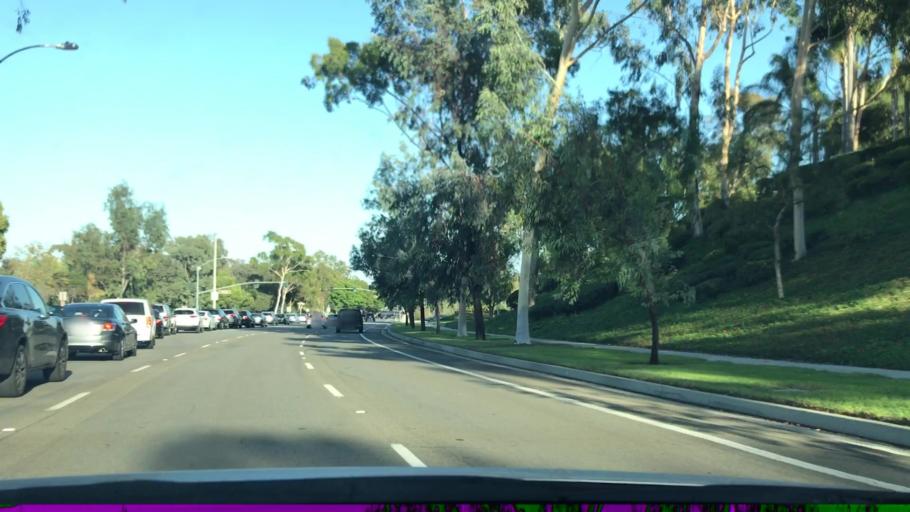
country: US
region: California
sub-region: Orange County
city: Irvine
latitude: 33.6575
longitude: -117.8405
